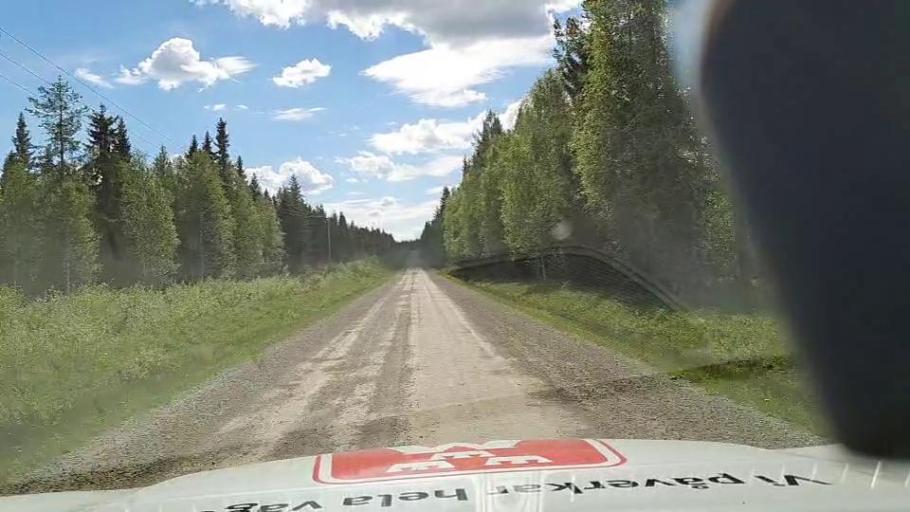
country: SE
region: Jaemtland
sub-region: Stroemsunds Kommun
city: Stroemsund
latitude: 64.5372
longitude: 15.6006
